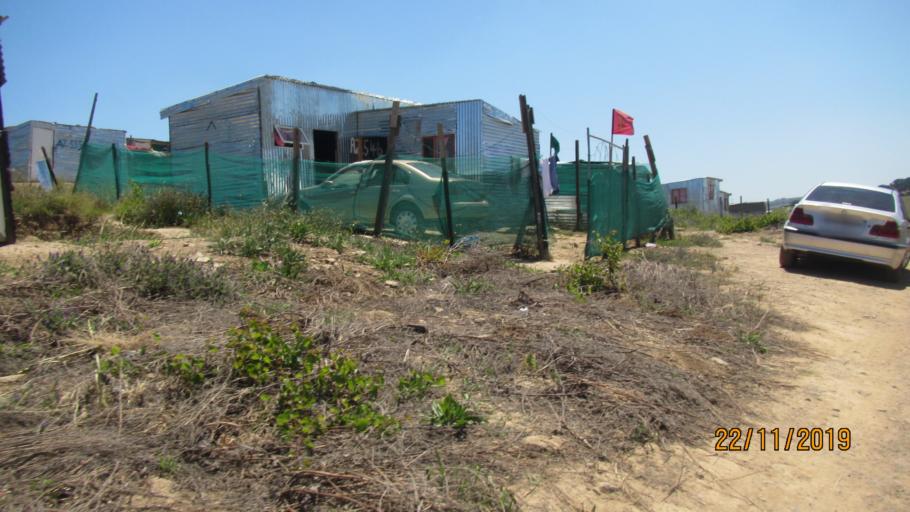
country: ZA
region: Western Cape
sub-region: Cape Winelands District Municipality
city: Stellenbosch
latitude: -33.9234
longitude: 18.8406
